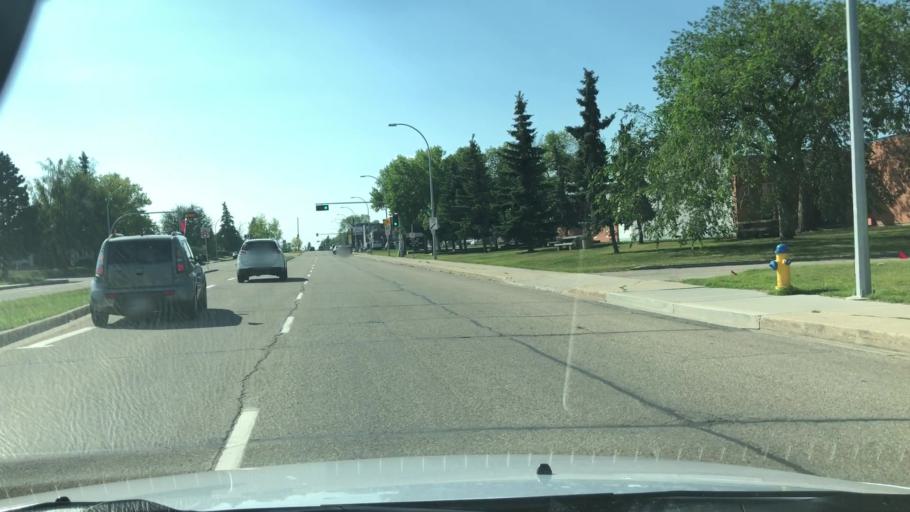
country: CA
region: Alberta
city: Edmonton
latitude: 53.6054
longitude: -113.4488
